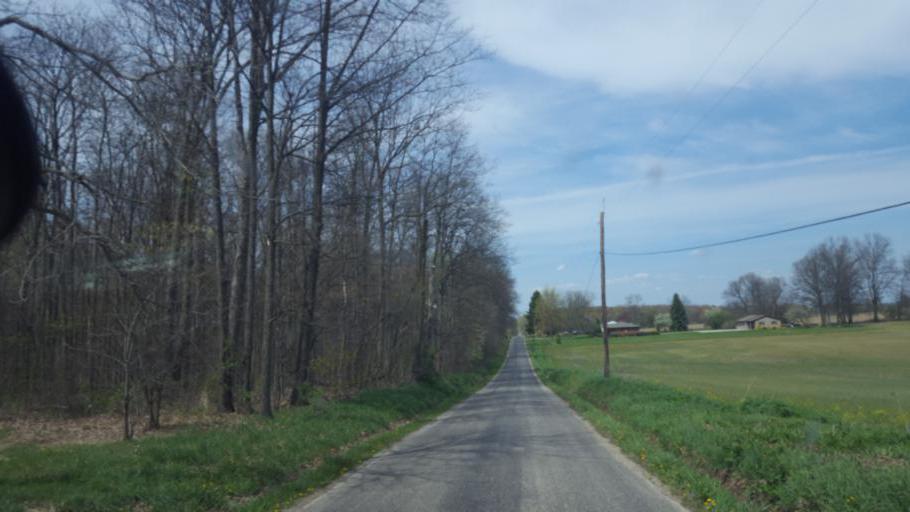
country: US
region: Ohio
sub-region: Ashland County
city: Ashland
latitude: 40.8857
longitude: -82.3781
